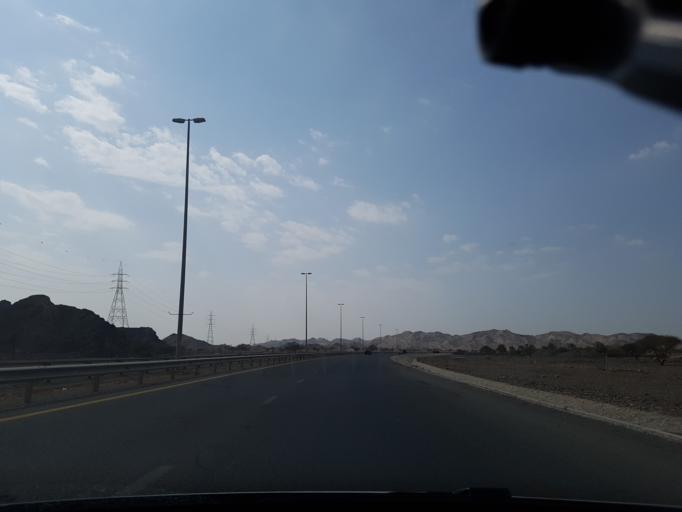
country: AE
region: Al Fujayrah
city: Dibba Al-Fujairah
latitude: 25.4911
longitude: 56.0426
